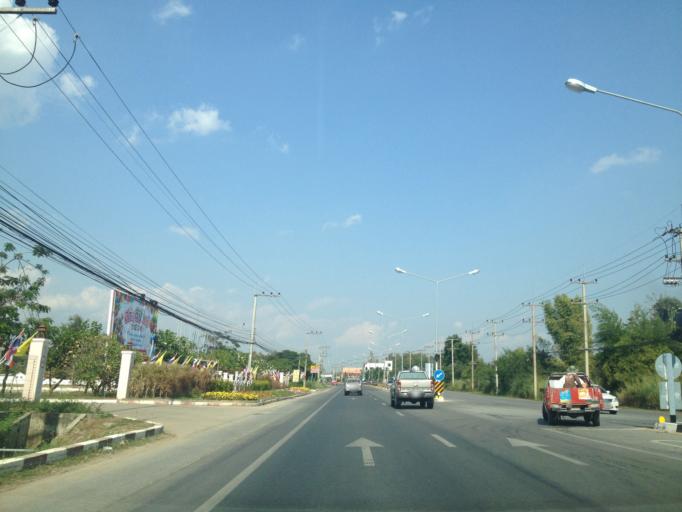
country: TH
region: Chiang Mai
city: San Pa Tong
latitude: 18.5747
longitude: 98.8799
